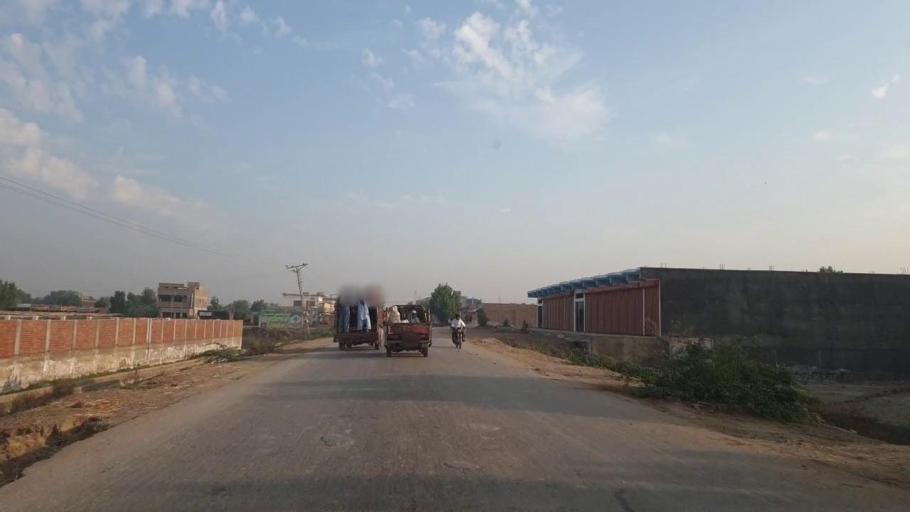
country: PK
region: Sindh
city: Tando Bago
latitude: 24.7776
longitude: 68.9616
